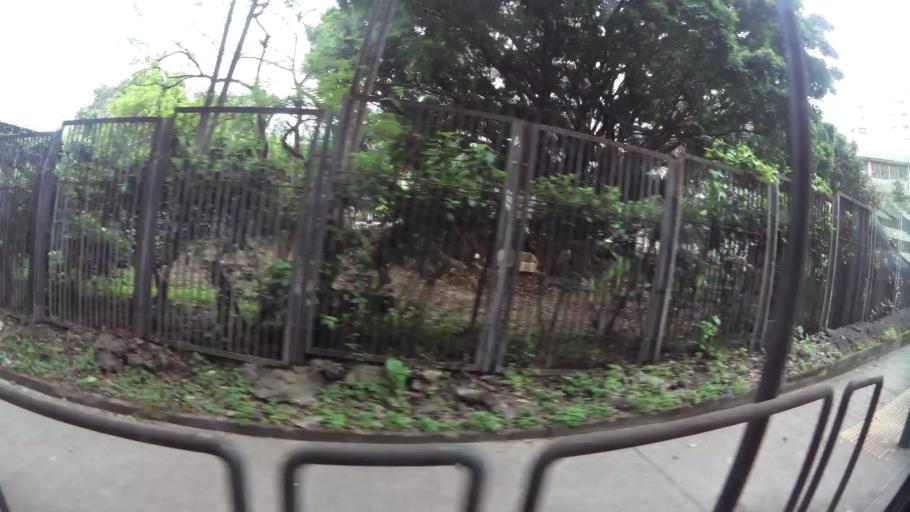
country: MO
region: Macau
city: Macau
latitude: 22.1623
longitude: 113.5594
